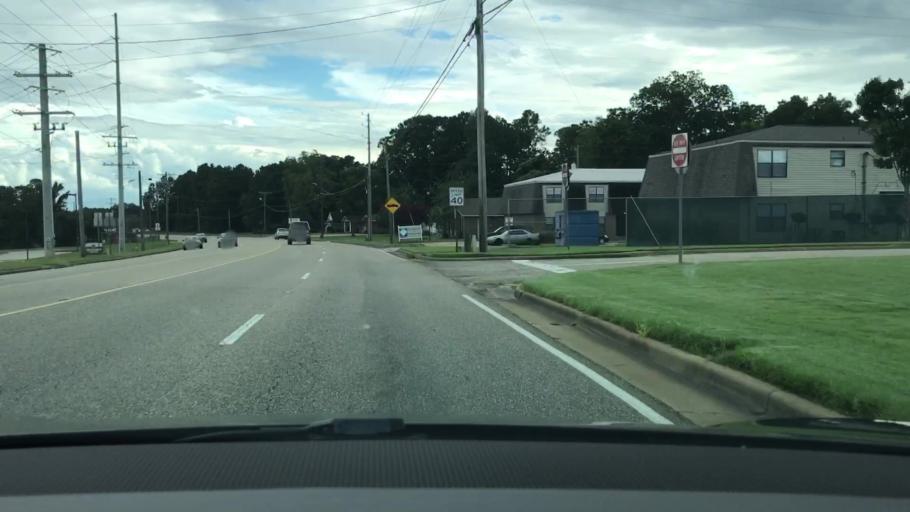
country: US
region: Alabama
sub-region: Pike County
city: Troy
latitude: 31.7824
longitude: -85.9645
